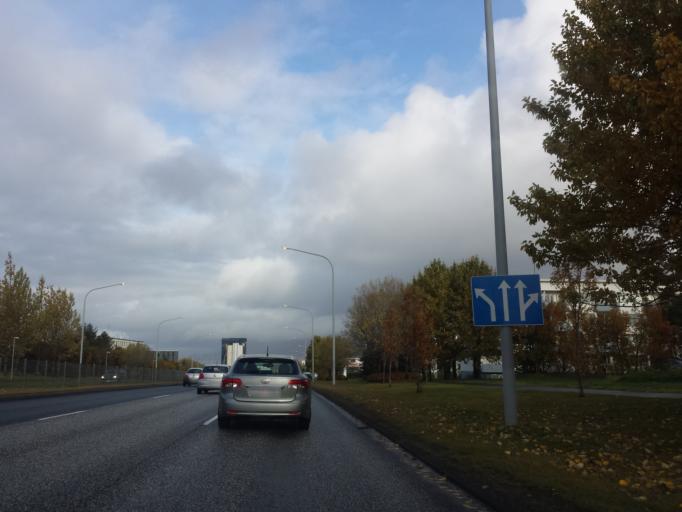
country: IS
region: Capital Region
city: Reykjavik
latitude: 64.1359
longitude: -21.8955
